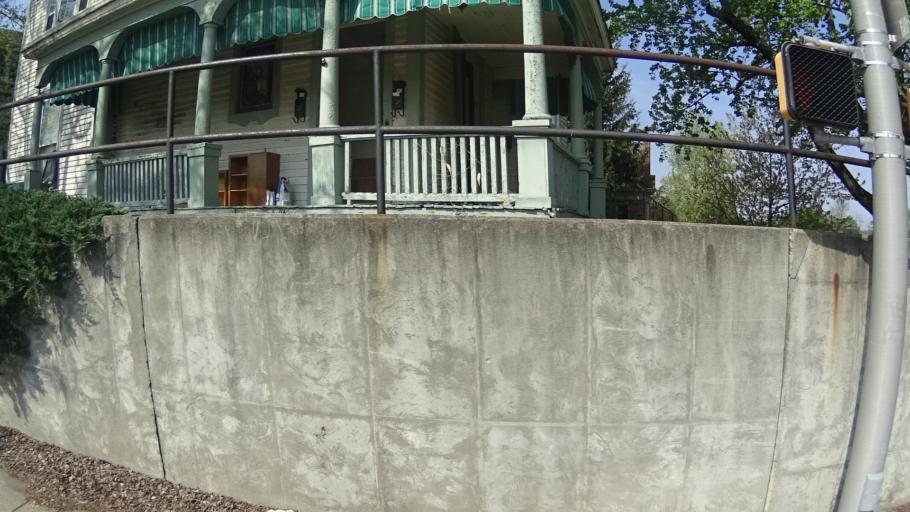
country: US
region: Indiana
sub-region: Madison County
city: Anderson
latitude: 40.1061
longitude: -85.6820
